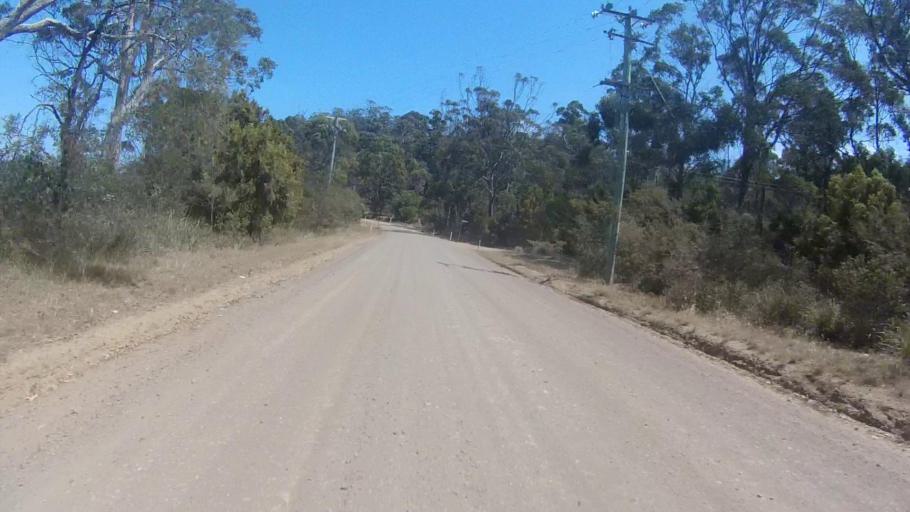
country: AU
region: Tasmania
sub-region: Sorell
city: Sorell
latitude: -42.8454
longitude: 147.8441
